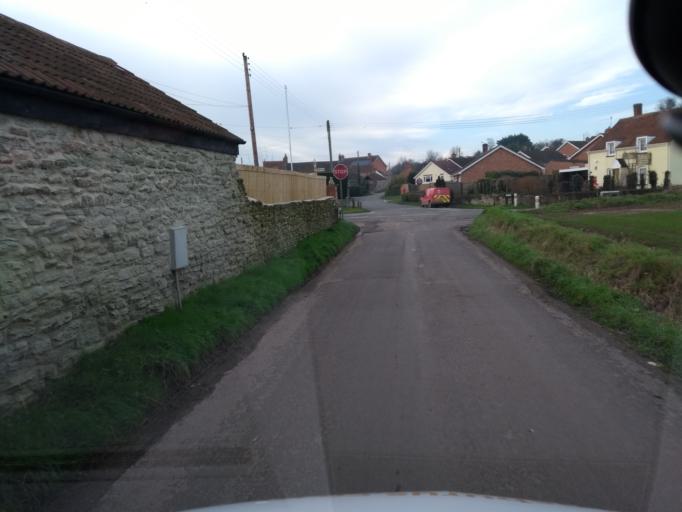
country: GB
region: England
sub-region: Somerset
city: Westonzoyland
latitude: 51.0948
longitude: -2.8906
